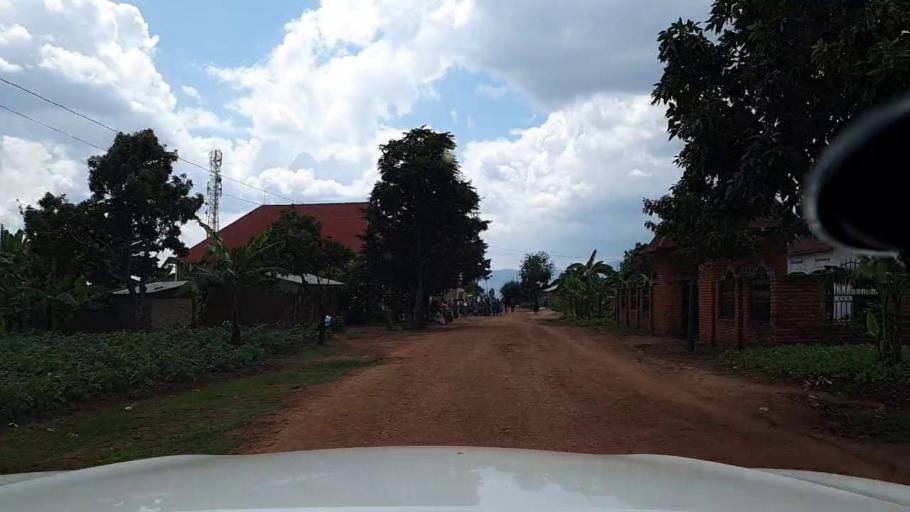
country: RW
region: Southern Province
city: Gitarama
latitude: -1.8379
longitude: 29.8311
